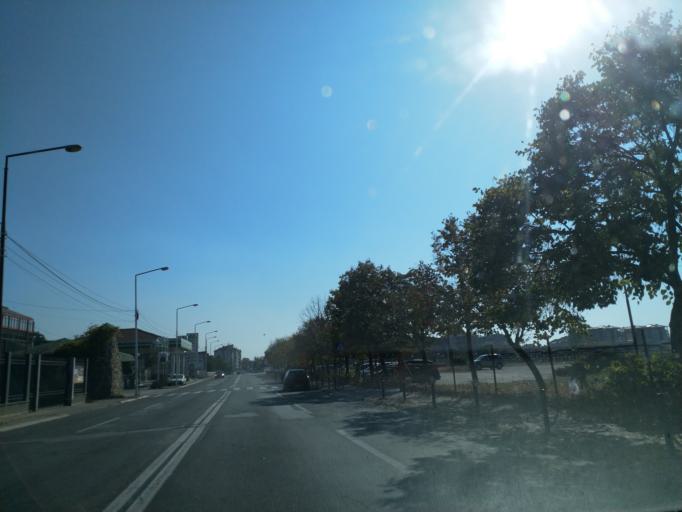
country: RS
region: Central Serbia
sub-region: Pomoravski Okrug
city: Paracin
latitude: 43.8639
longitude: 21.4209
